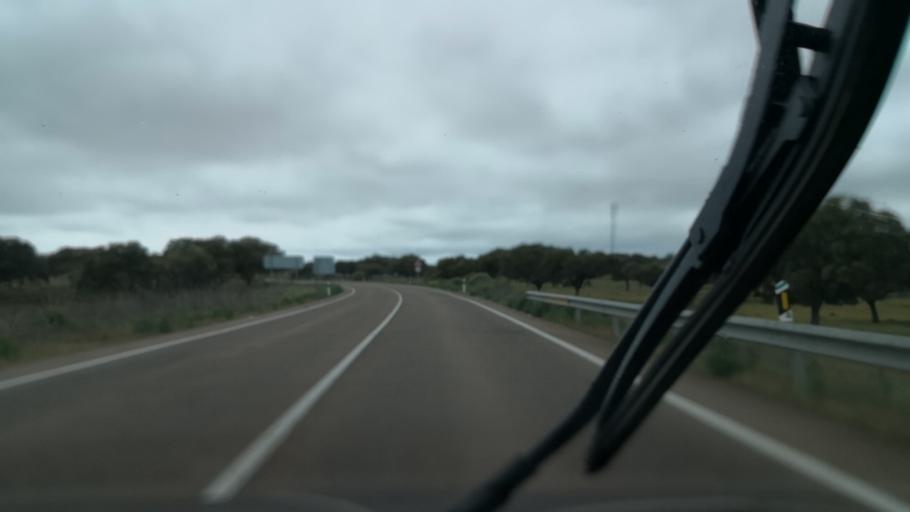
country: ES
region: Extremadura
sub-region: Provincia de Badajoz
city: Villar del Rey
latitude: 39.0332
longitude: -6.8238
